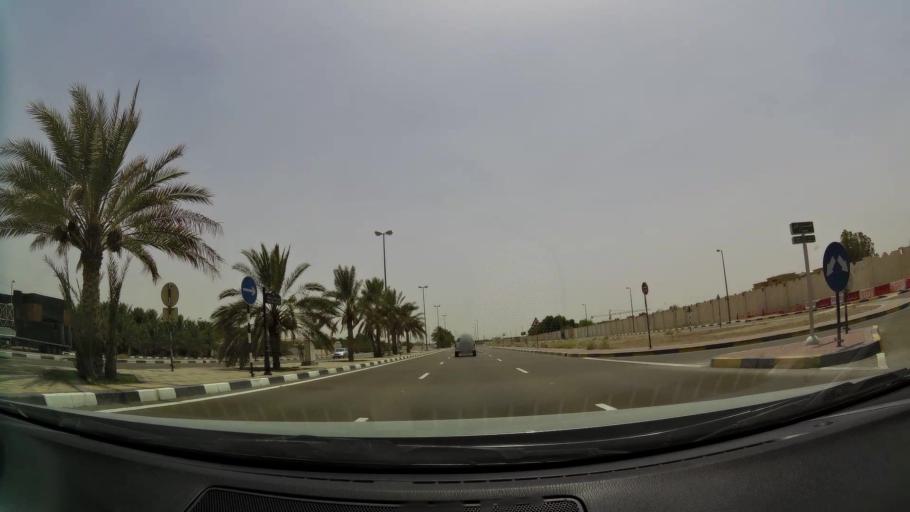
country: AE
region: Abu Dhabi
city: Al Ain
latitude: 24.1889
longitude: 55.6906
